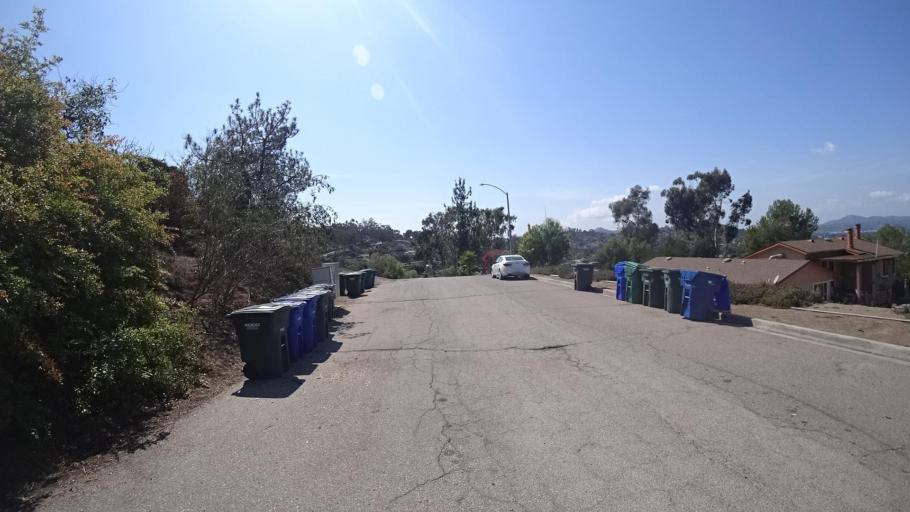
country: US
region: California
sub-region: San Diego County
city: Granite Hills
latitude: 32.7817
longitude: -116.9167
